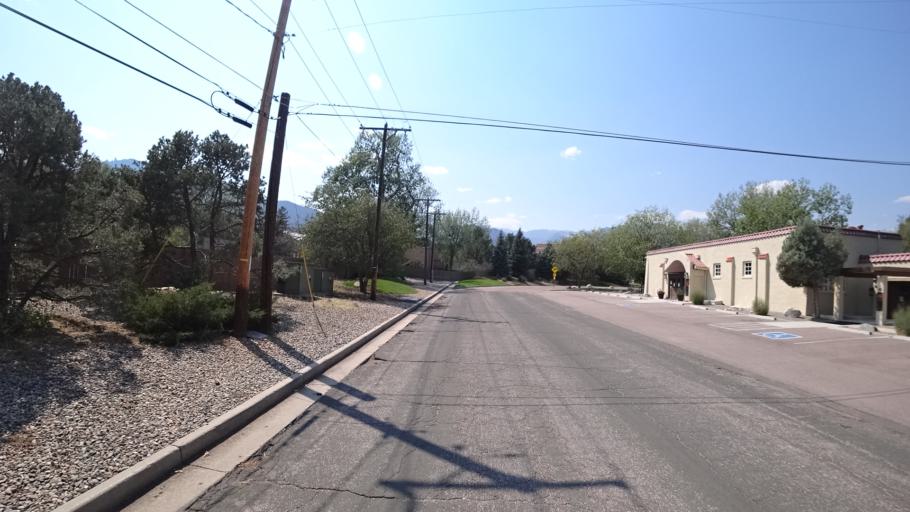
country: US
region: Colorado
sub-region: El Paso County
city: Colorado Springs
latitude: 38.7932
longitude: -104.8467
